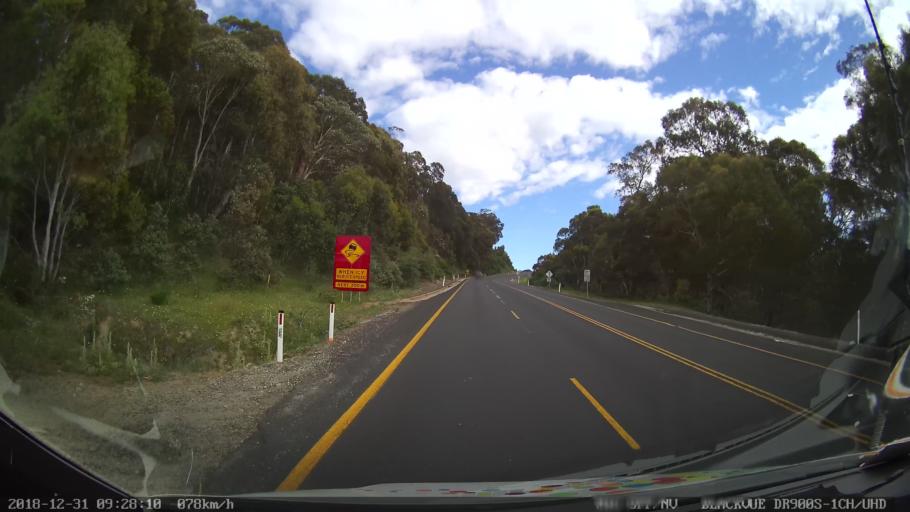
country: AU
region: New South Wales
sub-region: Snowy River
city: Jindabyne
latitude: -36.4584
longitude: 148.4758
